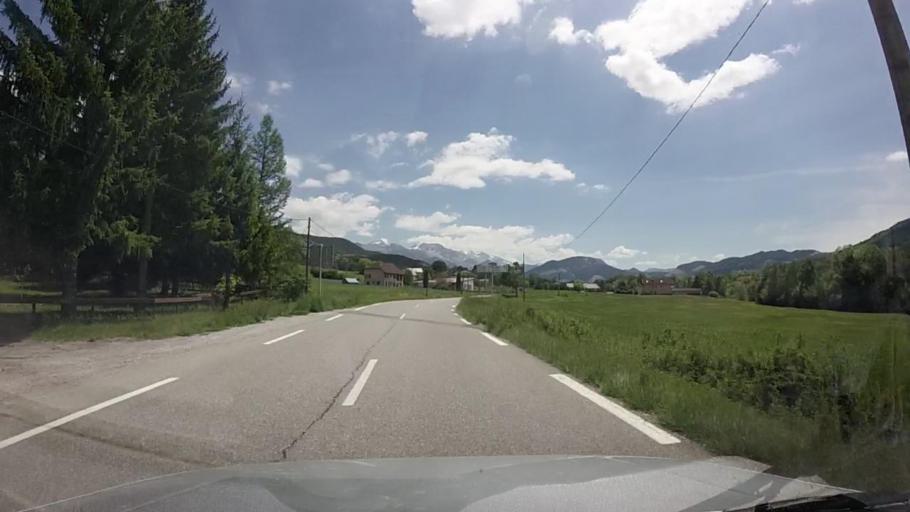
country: FR
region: Provence-Alpes-Cote d'Azur
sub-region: Departement des Alpes-de-Haute-Provence
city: Seyne-les-Alpes
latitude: 44.3696
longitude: 6.3168
